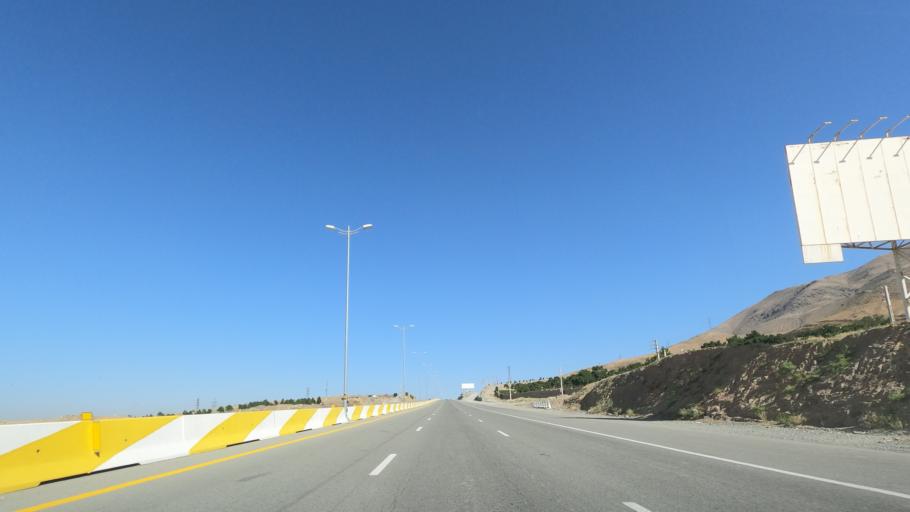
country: IR
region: Tehran
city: Shahr-e Qods
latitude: 35.7632
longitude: 51.0720
